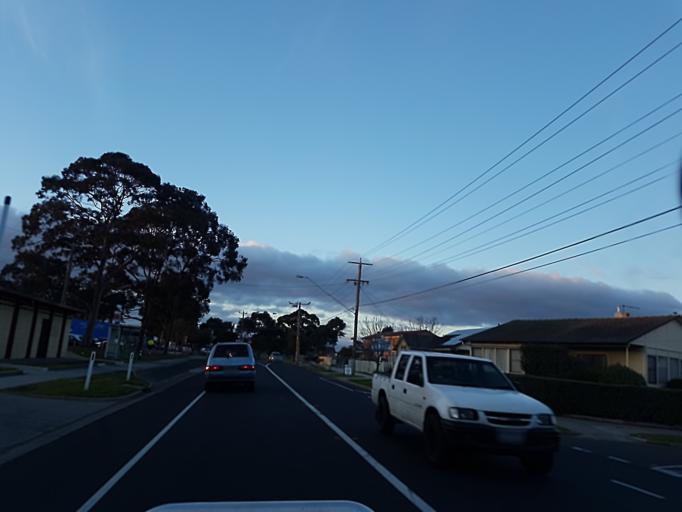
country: AU
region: Victoria
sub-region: Hume
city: Broadmeadows
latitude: -37.6736
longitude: 144.9310
